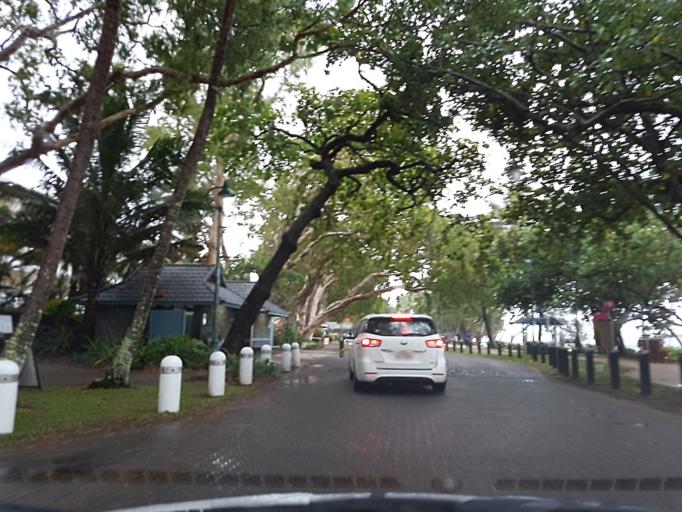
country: AU
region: Queensland
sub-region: Cairns
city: Palm Cove
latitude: -16.7433
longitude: 145.6708
